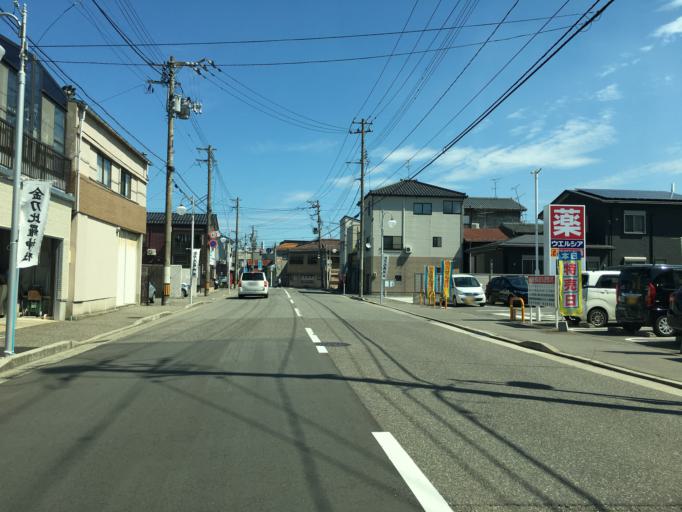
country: JP
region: Niigata
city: Niigata-shi
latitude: 37.9329
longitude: 139.0518
